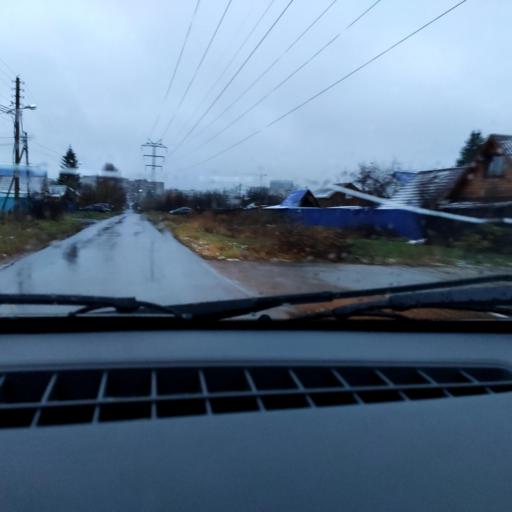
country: RU
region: Bashkortostan
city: Avdon
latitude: 54.6905
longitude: 55.8115
